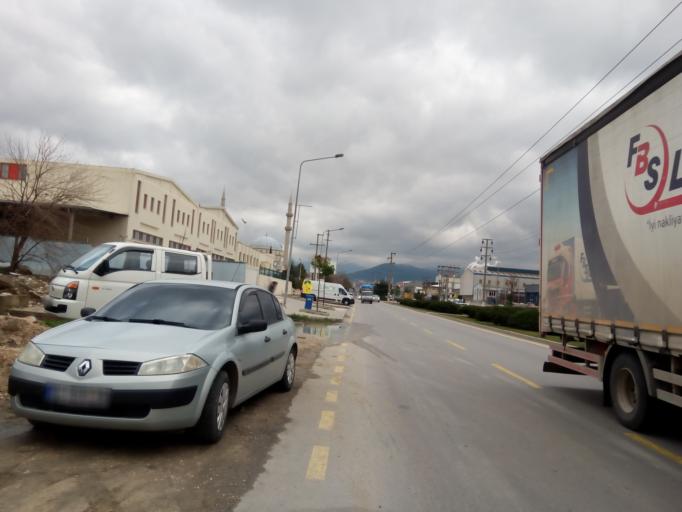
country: TR
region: Bursa
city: Niluefer
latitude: 40.2446
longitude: 28.9597
